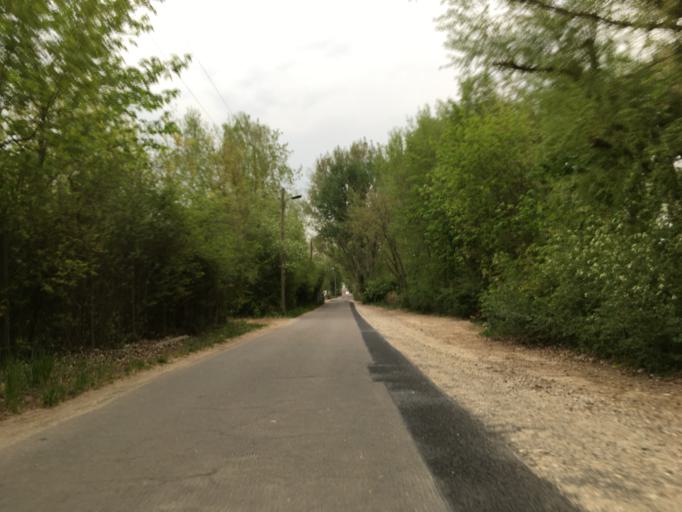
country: DE
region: Berlin
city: Wartenberg
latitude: 52.5822
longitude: 13.4983
